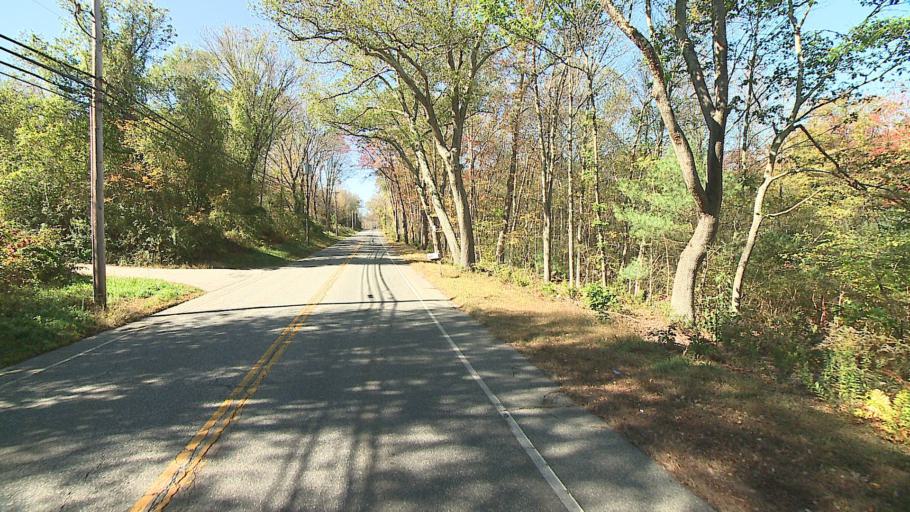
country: US
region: Connecticut
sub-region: Hartford County
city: Terramuggus
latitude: 41.6387
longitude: -72.4470
